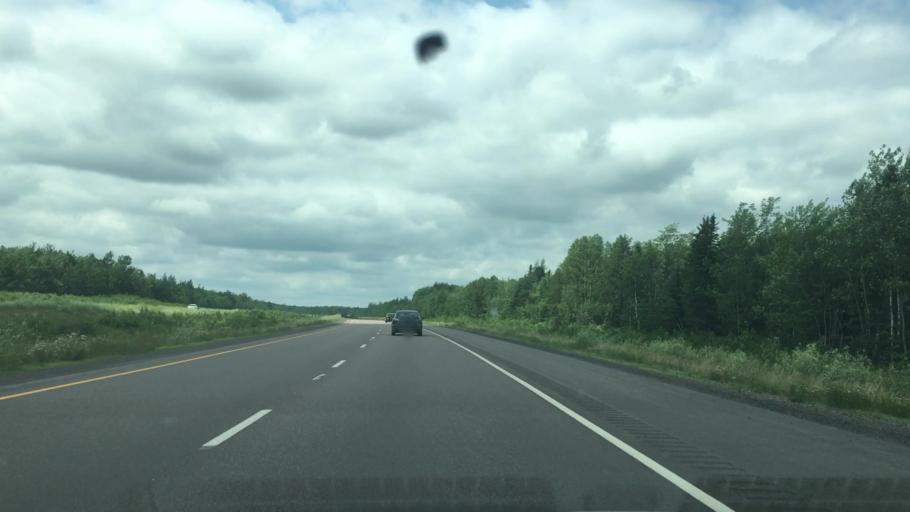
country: CA
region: New Brunswick
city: Dieppe
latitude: 46.1286
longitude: -64.6481
